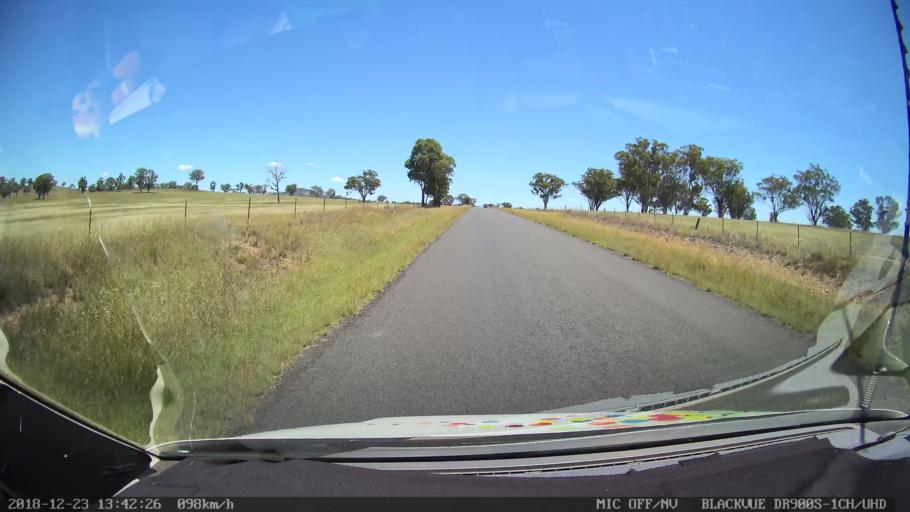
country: AU
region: New South Wales
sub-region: Armidale Dumaresq
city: Armidale
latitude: -30.4771
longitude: 151.1626
